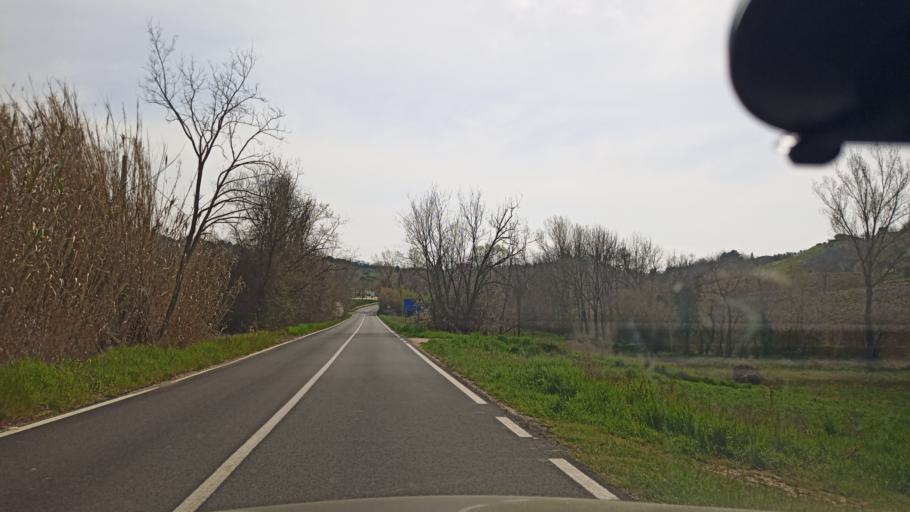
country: IT
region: Latium
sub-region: Provincia di Rieti
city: Cantalupo in Sabina
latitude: 42.3214
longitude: 12.6438
